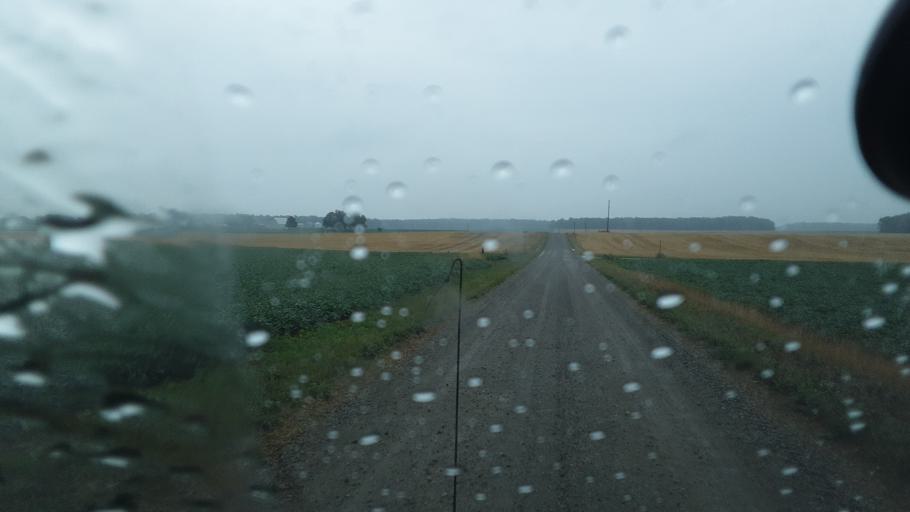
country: US
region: Indiana
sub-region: DeKalb County
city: Butler
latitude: 41.4164
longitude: -84.8130
